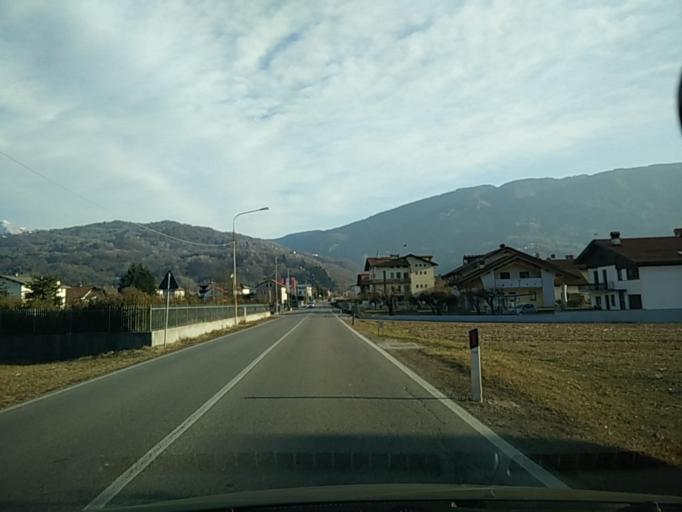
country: IT
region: Veneto
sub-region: Provincia di Belluno
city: Farra d'Alpago
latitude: 46.1311
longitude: 12.3444
